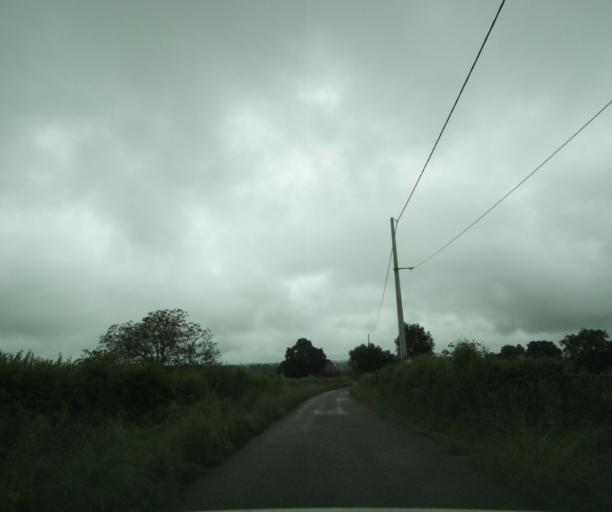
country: FR
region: Bourgogne
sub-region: Departement de Saone-et-Loire
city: Charolles
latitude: 46.4294
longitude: 4.3507
